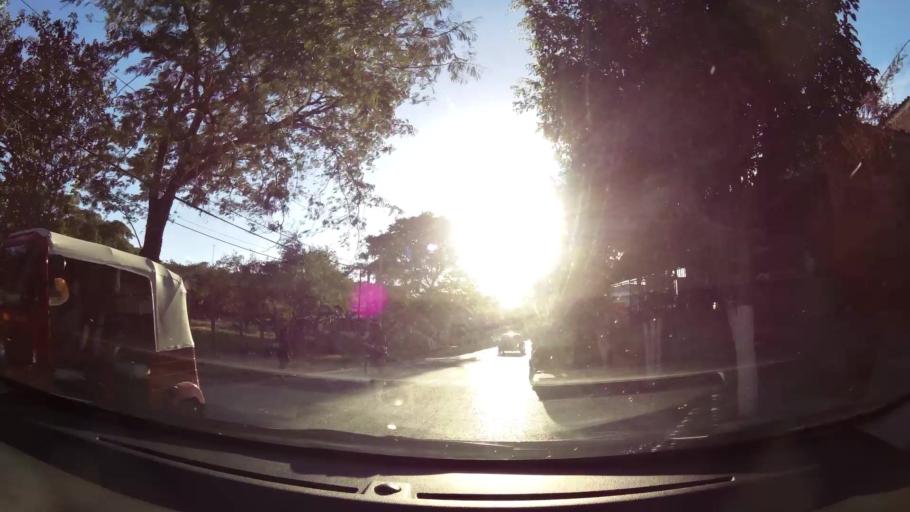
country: SV
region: Santa Ana
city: Metapan
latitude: 14.3298
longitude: -89.4510
